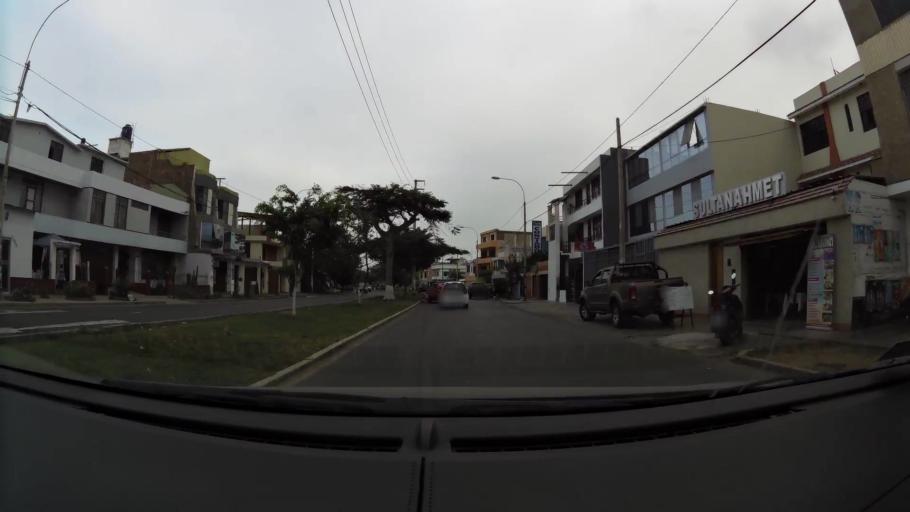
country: PE
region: La Libertad
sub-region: Provincia de Trujillo
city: Trujillo
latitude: -8.0980
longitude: -79.0302
